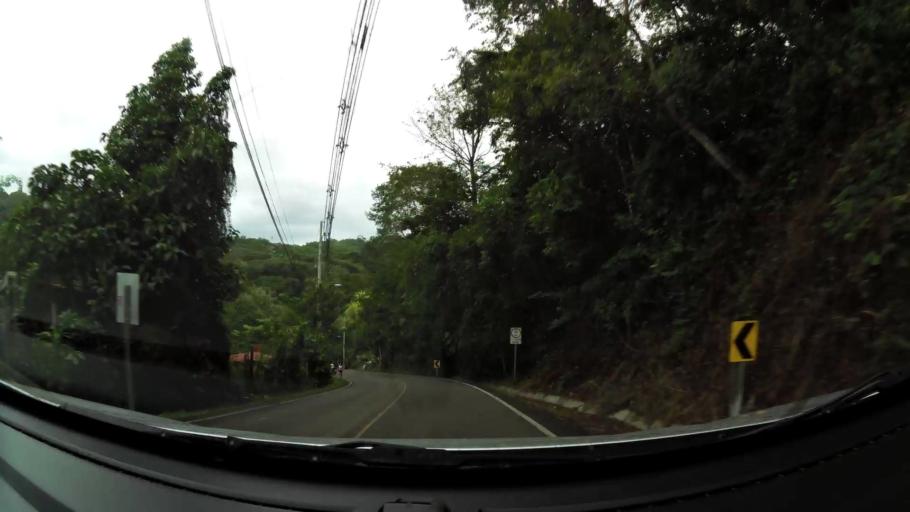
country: CR
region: Puntarenas
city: Esparza
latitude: 9.9602
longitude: -84.6078
